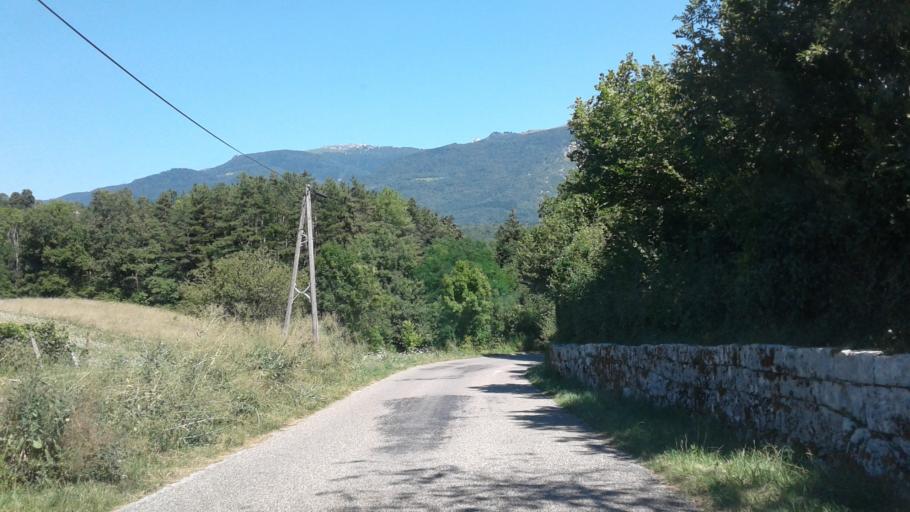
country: FR
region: Rhone-Alpes
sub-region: Departement de l'Ain
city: Artemare
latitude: 45.8745
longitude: 5.6742
